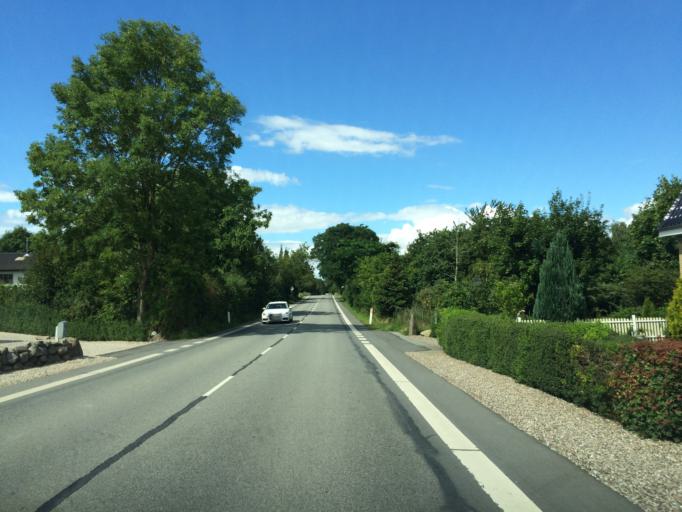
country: DK
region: South Denmark
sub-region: Faaborg-Midtfyn Kommune
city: Faaborg
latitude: 55.1144
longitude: 10.2195
